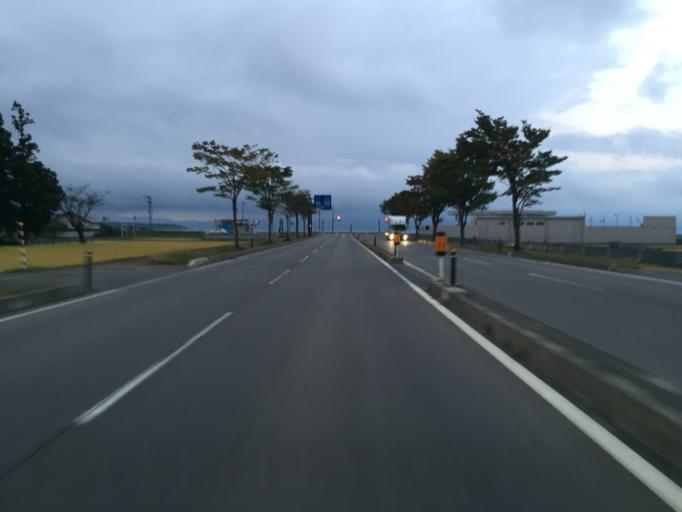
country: JP
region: Fukushima
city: Inawashiro
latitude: 37.5365
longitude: 140.1082
